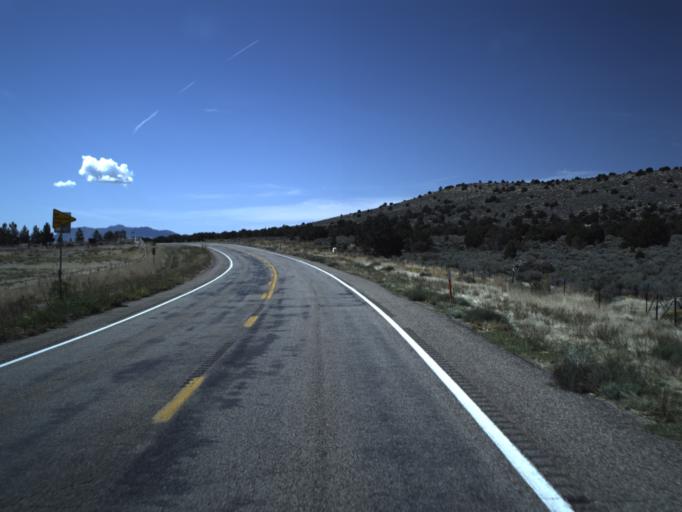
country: US
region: Utah
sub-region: Washington County
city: Ivins
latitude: 37.3705
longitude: -113.6637
